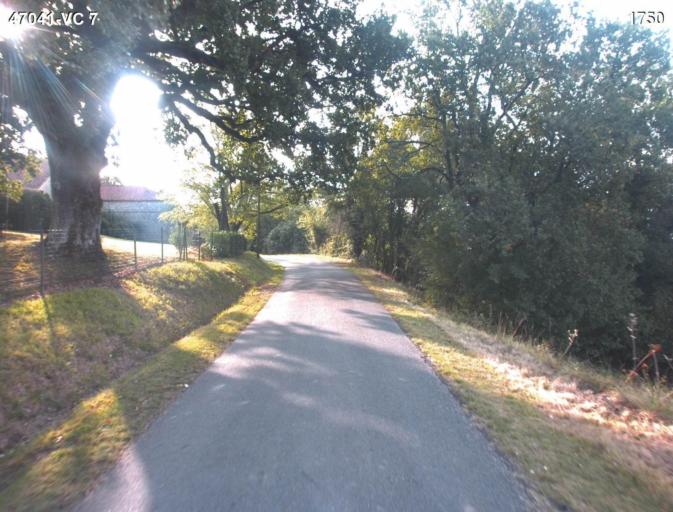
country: FR
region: Aquitaine
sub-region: Departement du Lot-et-Garonne
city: Port-Sainte-Marie
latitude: 44.1947
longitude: 0.4186
